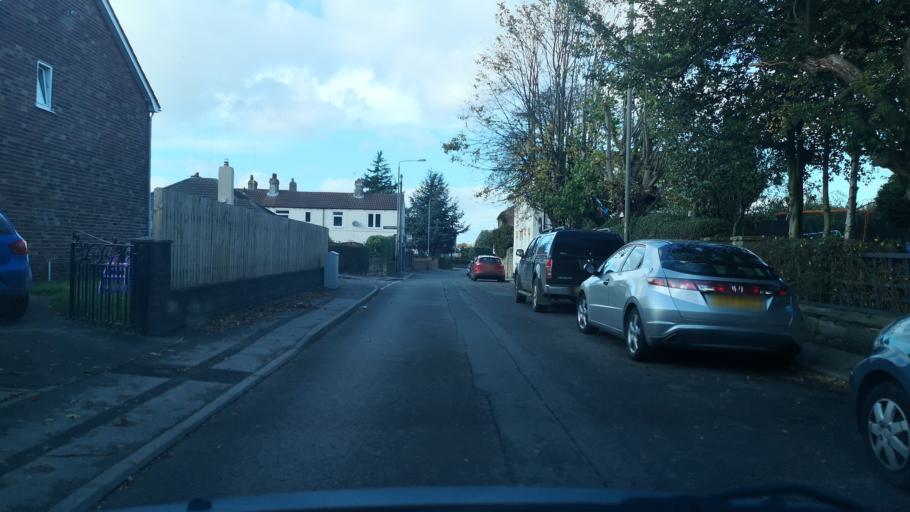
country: GB
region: England
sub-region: City and Borough of Wakefield
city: Featherstone
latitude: 53.6731
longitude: -1.3511
